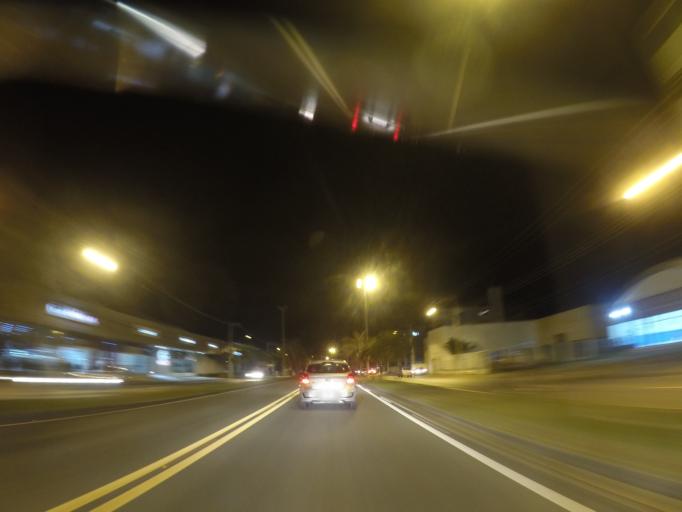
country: BR
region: Espirito Santo
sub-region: Linhares
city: Linhares
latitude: -19.4011
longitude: -40.0616
